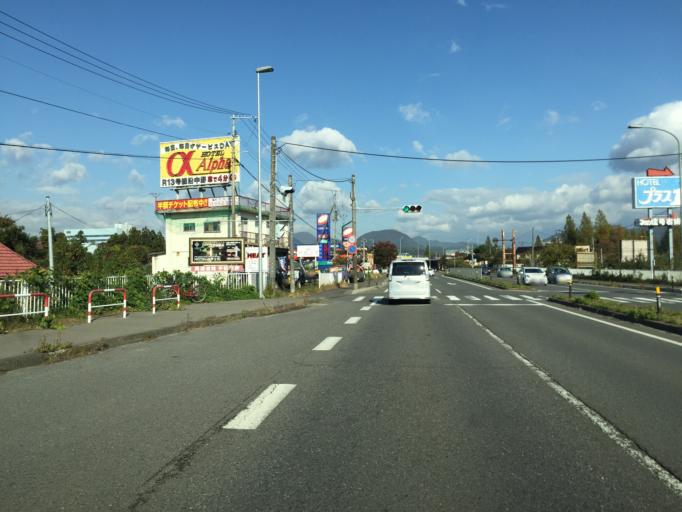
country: JP
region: Fukushima
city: Fukushima-shi
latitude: 37.7996
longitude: 140.4553
